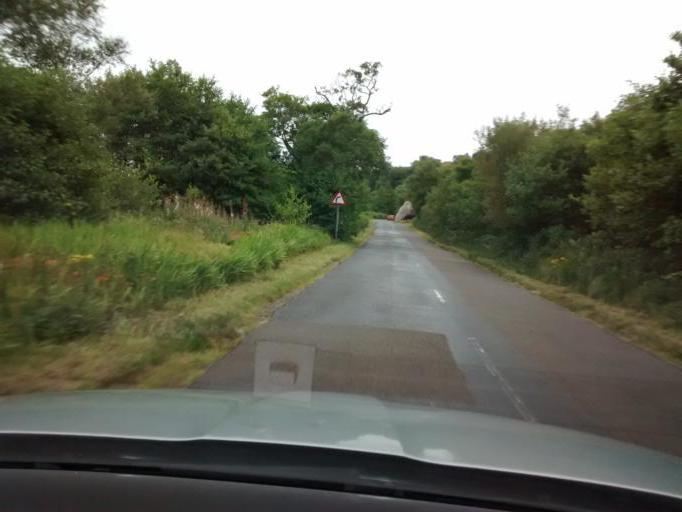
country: GB
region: Scotland
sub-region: North Ayrshire
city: Isle of Arran
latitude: 55.6549
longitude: -5.1483
